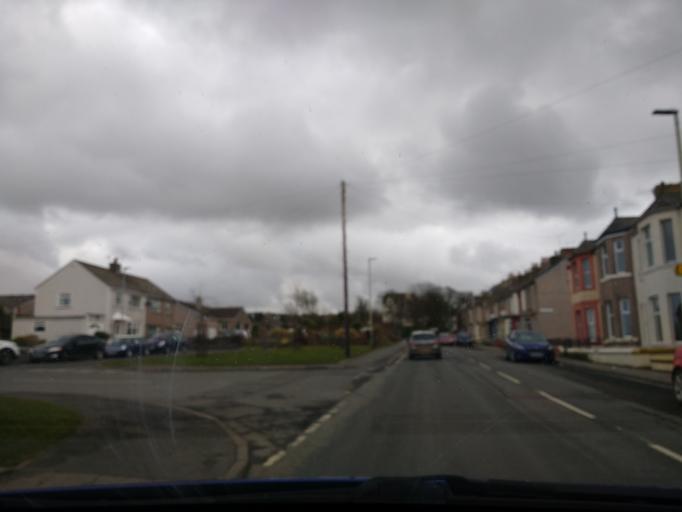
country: GB
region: England
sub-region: Cumbria
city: Maryport
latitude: 54.7115
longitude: -3.4868
